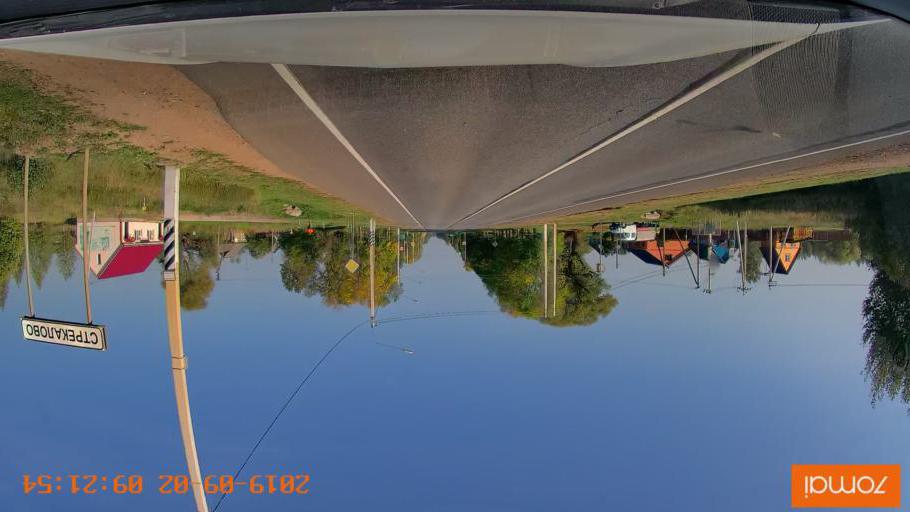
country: RU
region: Kaluga
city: Yukhnov
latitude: 54.7882
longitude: 35.3488
